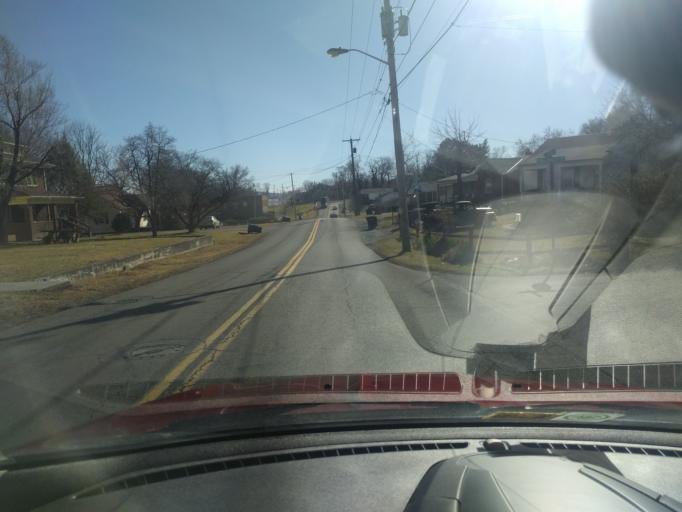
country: US
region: Virginia
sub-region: City of Roanoke
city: Roanoke
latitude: 37.3006
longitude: -79.9311
